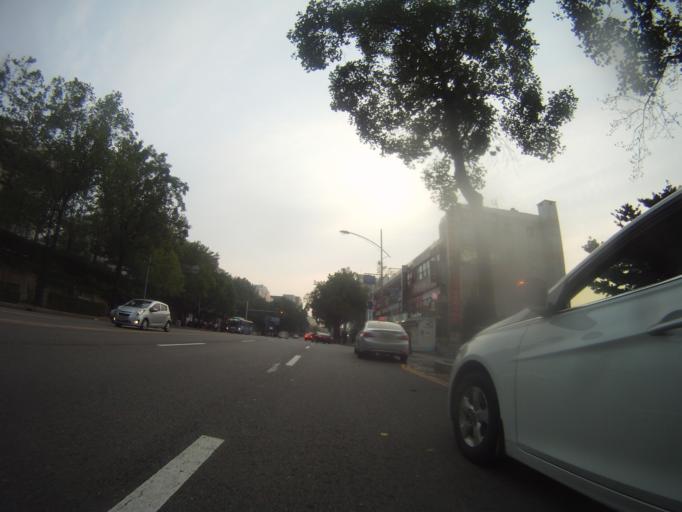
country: KR
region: Incheon
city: Incheon
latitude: 37.4574
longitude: 126.6942
